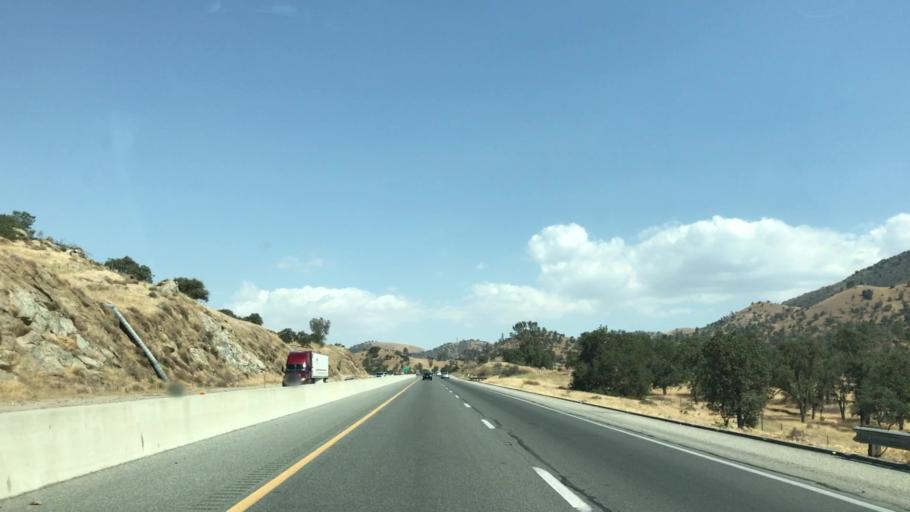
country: US
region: California
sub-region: Kern County
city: Golden Hills
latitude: 35.2062
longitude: -118.5335
